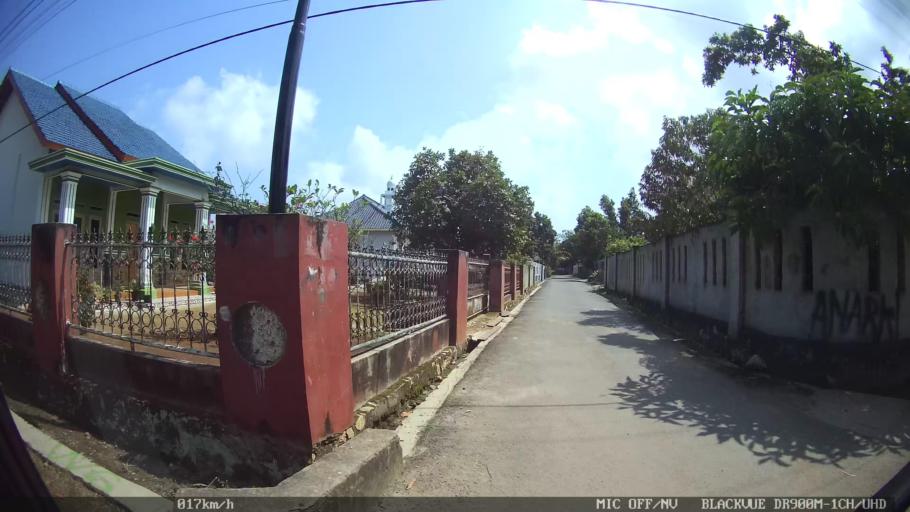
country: ID
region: Lampung
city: Kedaton
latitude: -5.3450
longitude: 105.2939
